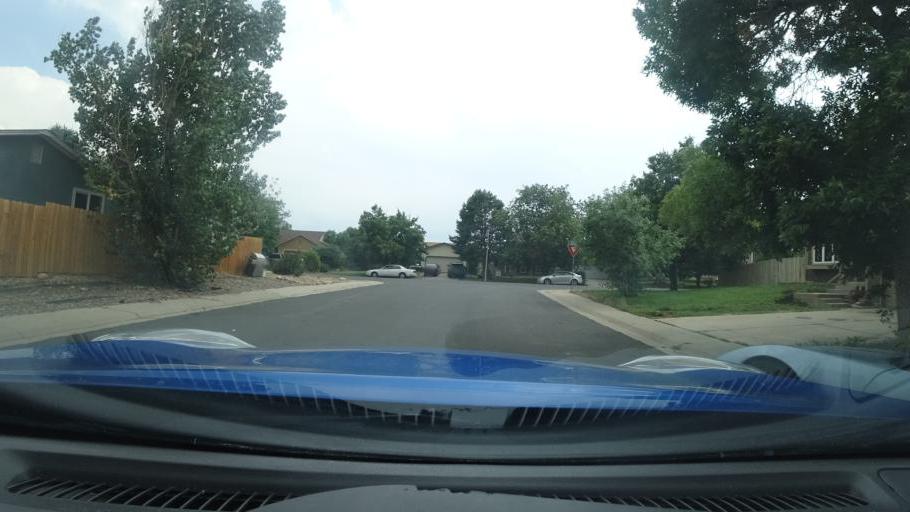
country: US
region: Colorado
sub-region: Adams County
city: Aurora
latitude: 39.6829
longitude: -104.7578
